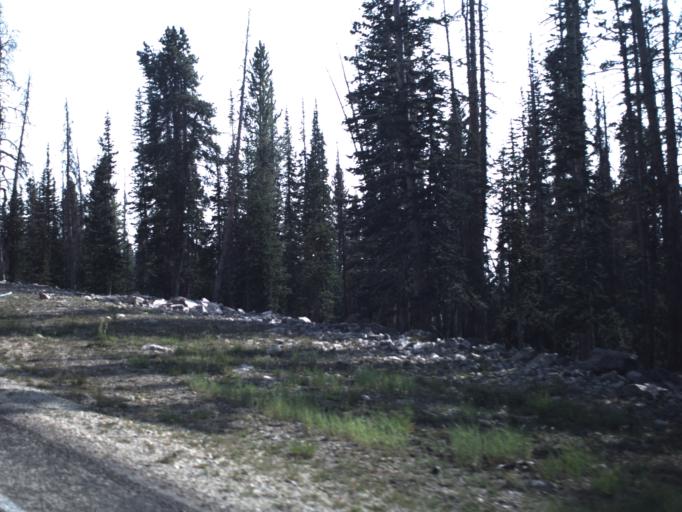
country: US
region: Utah
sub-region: Summit County
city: Kamas
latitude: 40.6826
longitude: -110.9277
